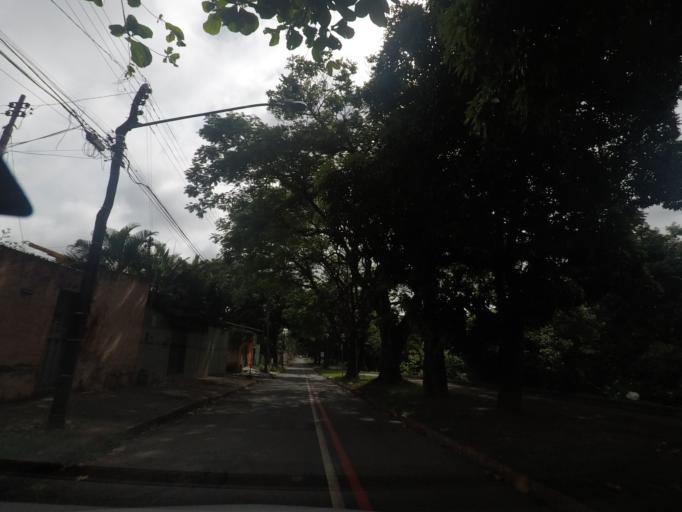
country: BR
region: Goias
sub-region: Goiania
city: Goiania
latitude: -16.7257
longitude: -49.2568
